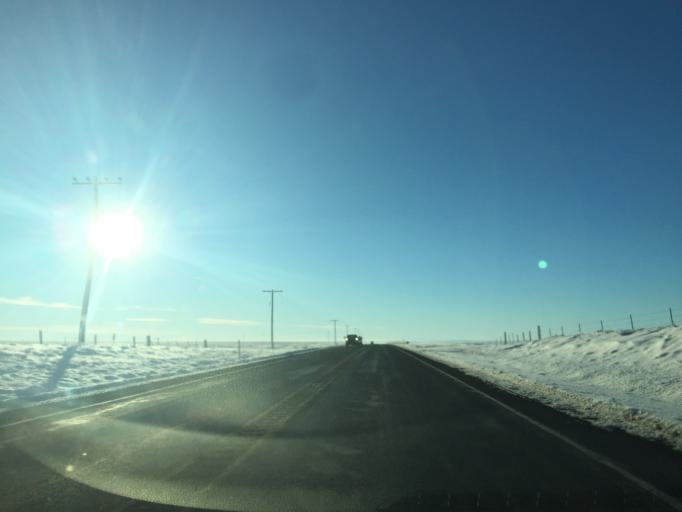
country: US
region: Washington
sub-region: Okanogan County
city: Coulee Dam
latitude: 47.7345
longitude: -118.8570
